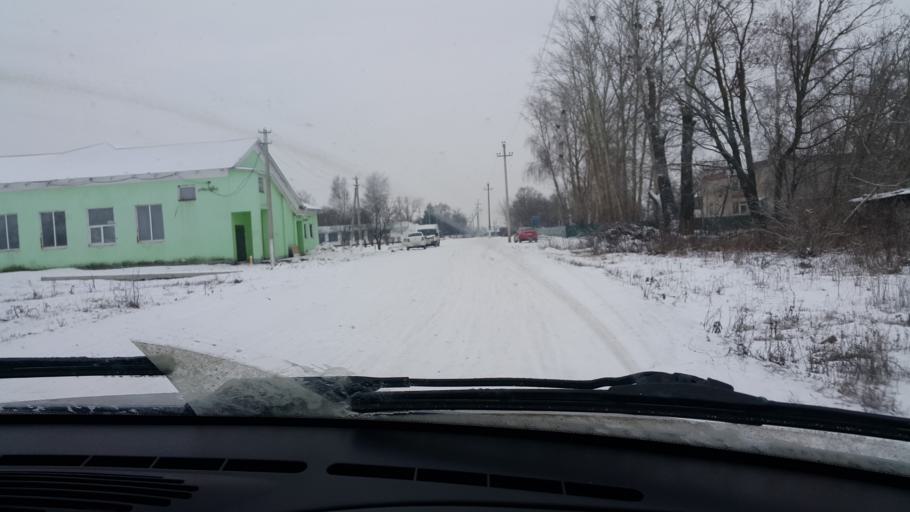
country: RU
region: Tambov
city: Inzhavino
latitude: 52.4692
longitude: 42.3823
